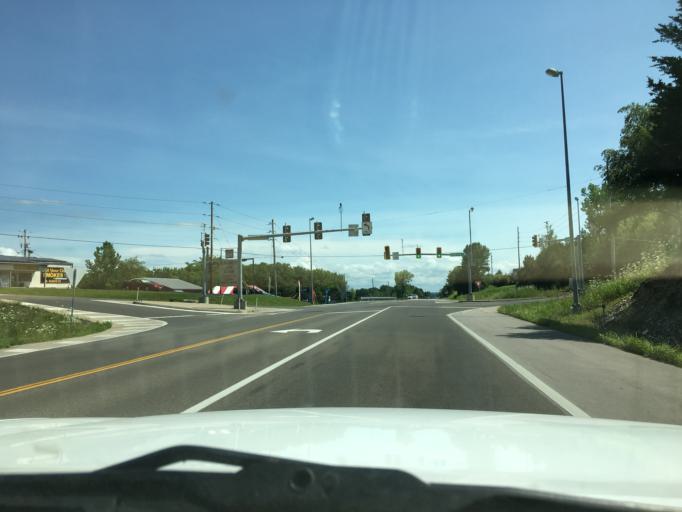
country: US
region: Missouri
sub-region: Franklin County
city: Union
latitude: 38.4827
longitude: -91.0052
